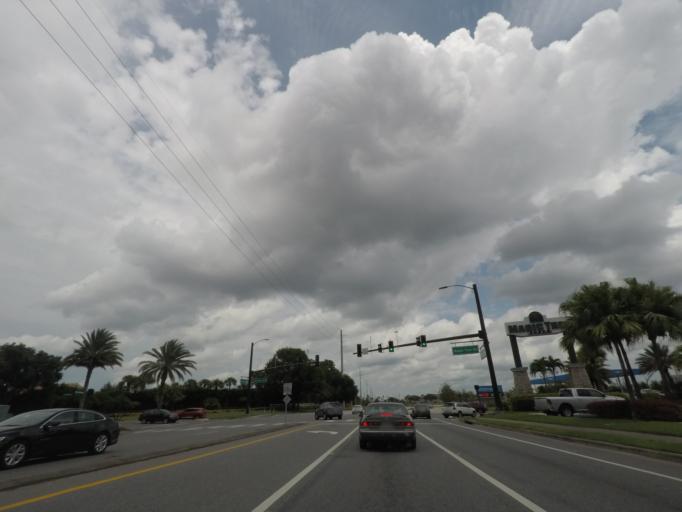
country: US
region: Florida
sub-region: Polk County
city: Citrus Ridge
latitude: 28.3285
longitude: -81.5903
